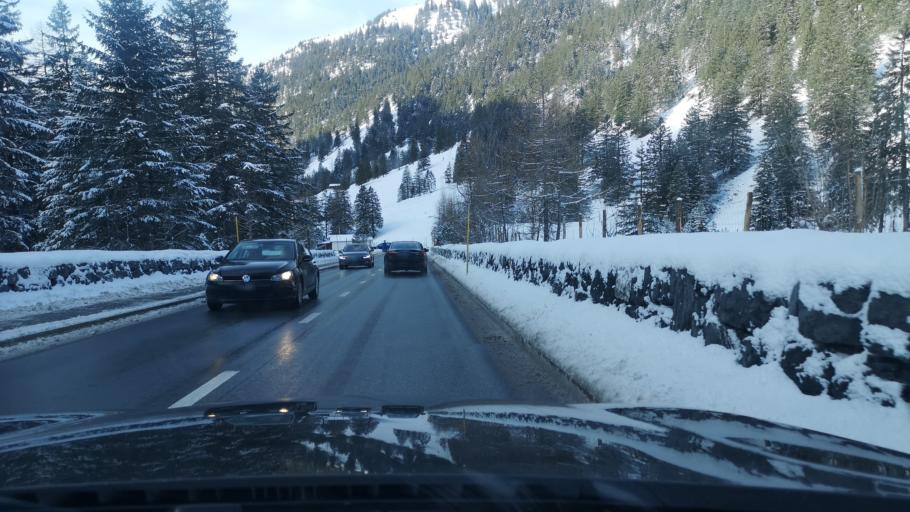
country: LI
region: Triesenberg
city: Triesenberg
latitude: 47.1094
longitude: 9.5980
